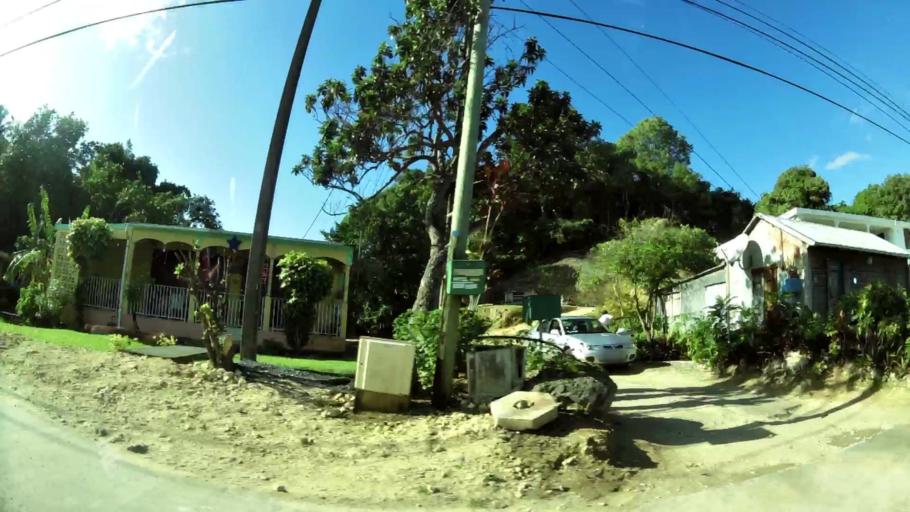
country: GP
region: Guadeloupe
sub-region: Guadeloupe
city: Petit-Canal
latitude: 16.3242
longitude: -61.4432
